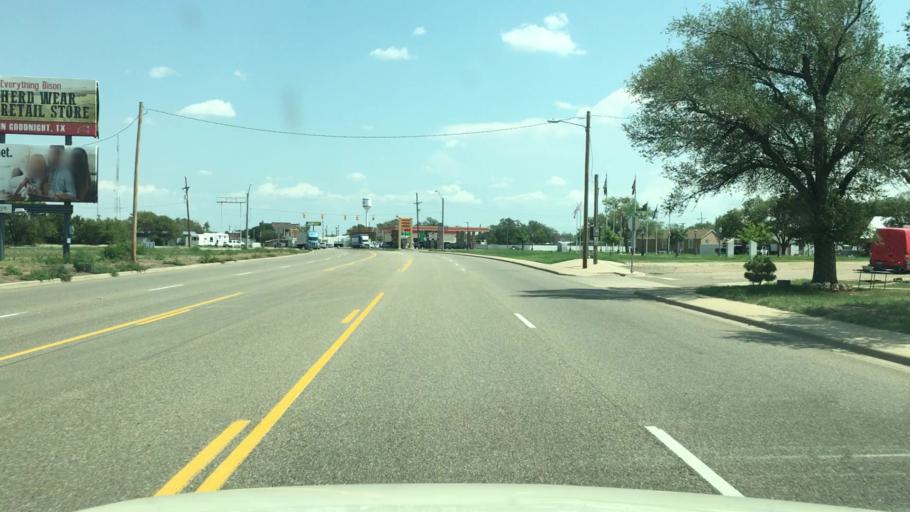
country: US
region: Texas
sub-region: Armstrong County
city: Claude
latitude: 35.1127
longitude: -101.3651
